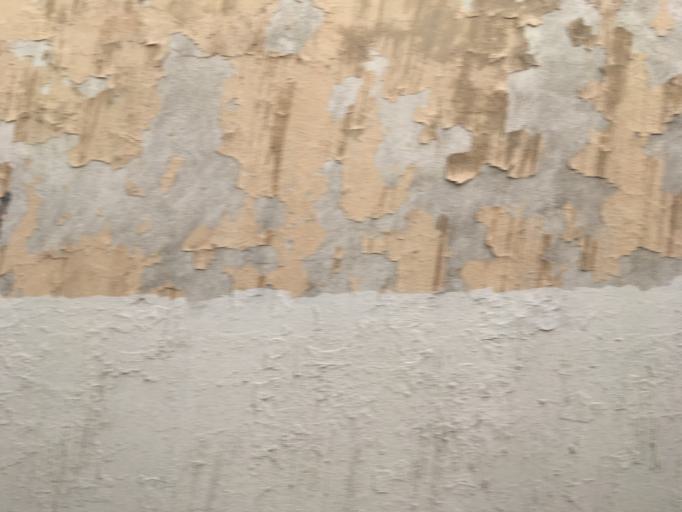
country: BR
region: Rio de Janeiro
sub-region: Rio De Janeiro
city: Rio de Janeiro
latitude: -22.9015
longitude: -43.2547
